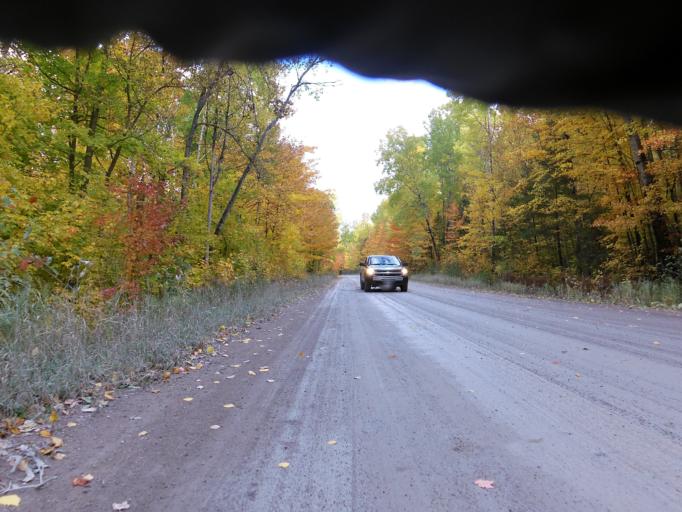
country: CA
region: Ontario
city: Petawawa
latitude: 45.8100
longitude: -77.3608
